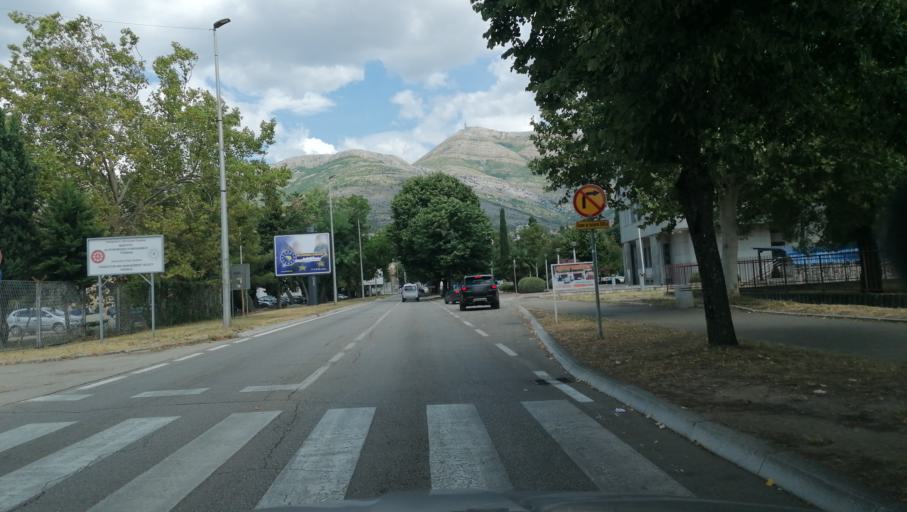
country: BA
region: Republika Srpska
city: Trebinje
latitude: 42.7085
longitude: 18.3426
